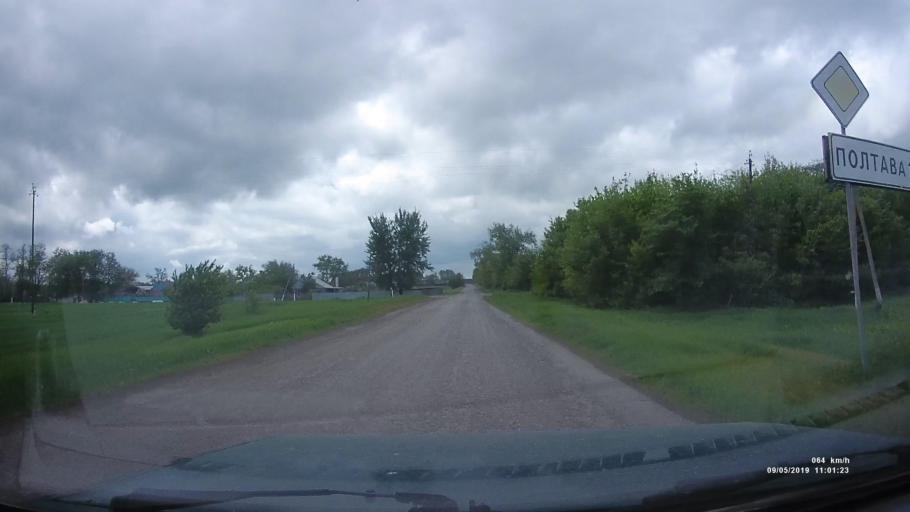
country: RU
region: Rostov
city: Peshkovo
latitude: 46.8495
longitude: 39.2153
